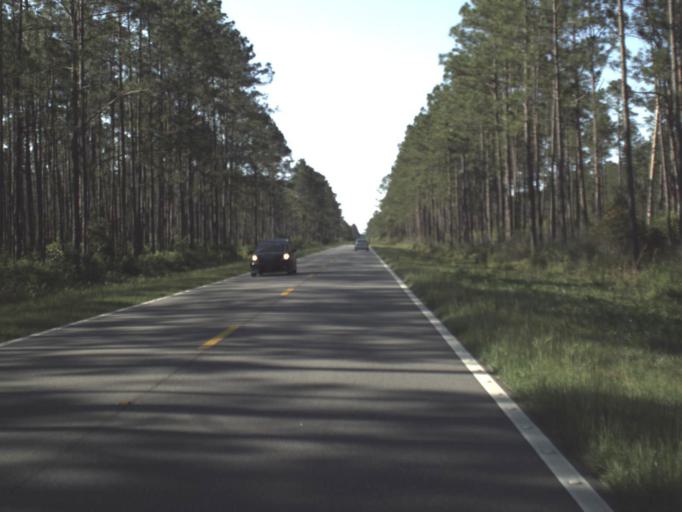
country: US
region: Florida
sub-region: Gulf County
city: Wewahitchka
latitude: 30.0983
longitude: -84.9853
